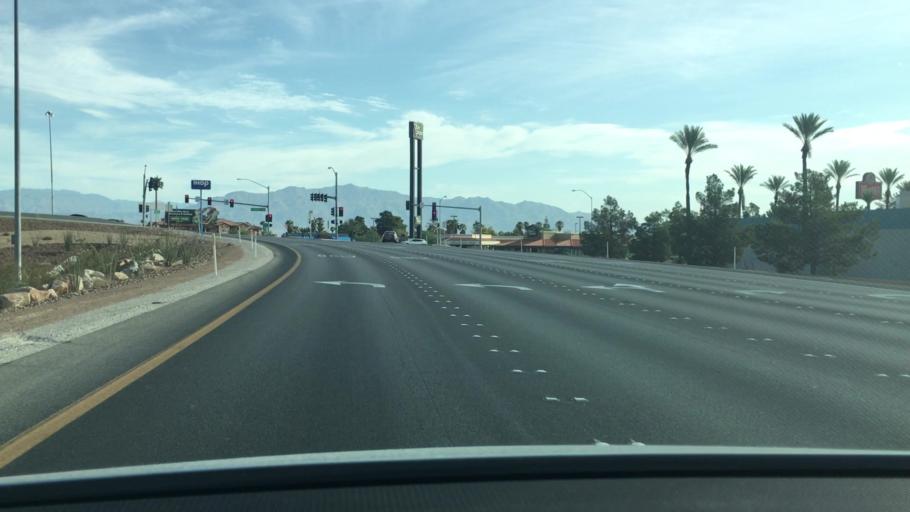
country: US
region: Nevada
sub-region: Clark County
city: Spring Valley
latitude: 36.2171
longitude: -115.2457
